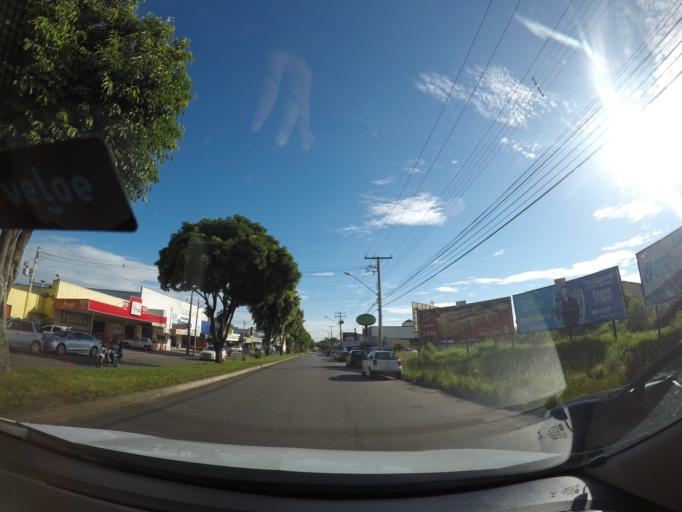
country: BR
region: Goias
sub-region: Goiania
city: Goiania
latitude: -16.7345
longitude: -49.3070
